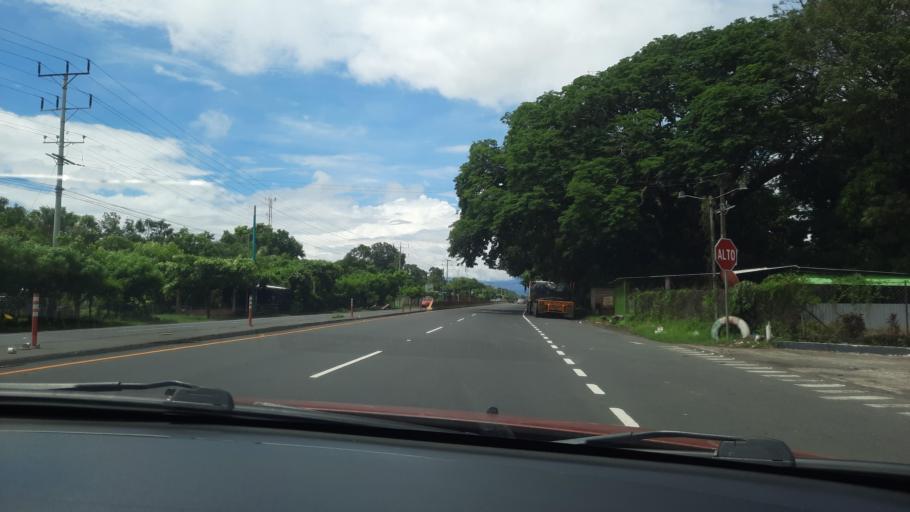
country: SV
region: Sonsonate
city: Acajutla
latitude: 13.6293
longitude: -89.7849
